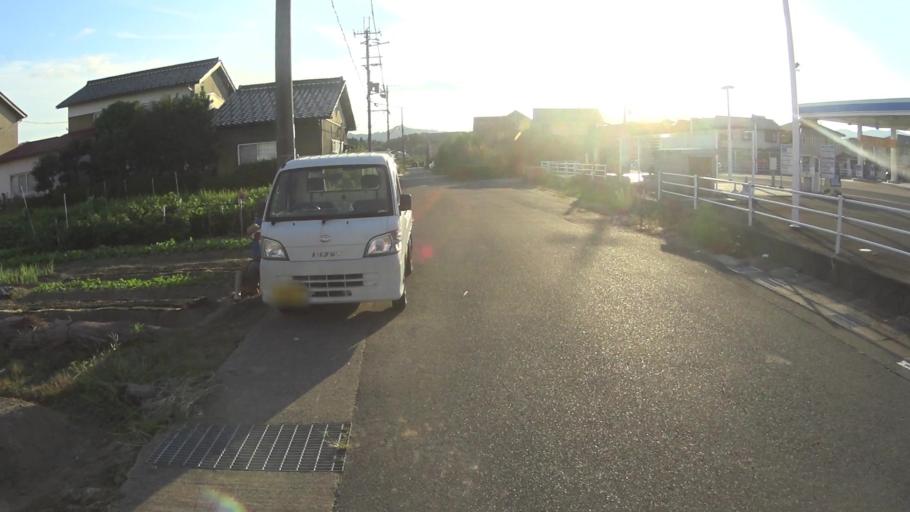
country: JP
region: Kyoto
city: Miyazu
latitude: 35.6068
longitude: 135.0815
